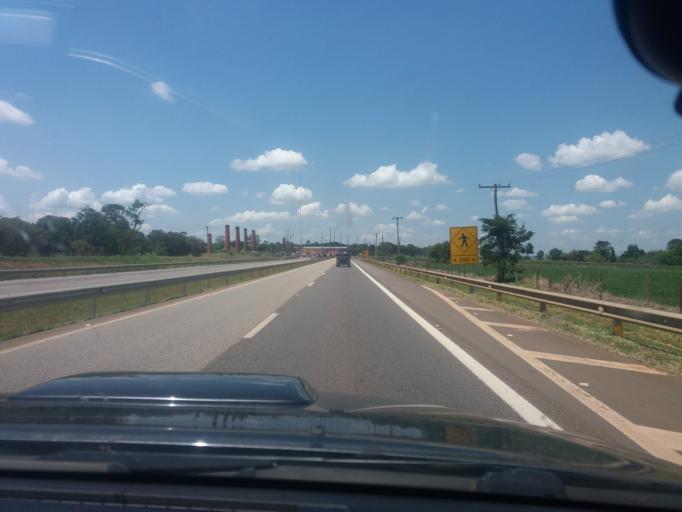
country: BR
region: Sao Paulo
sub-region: Tatui
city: Tatui
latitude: -23.4309
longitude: -47.9361
